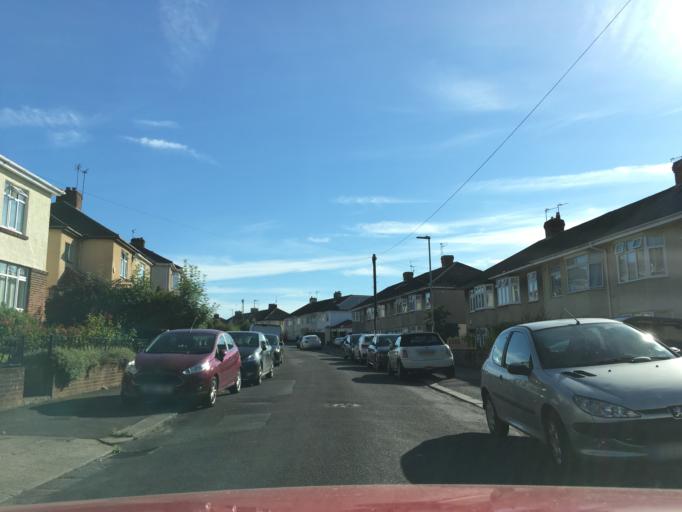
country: GB
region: England
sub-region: Bath and North East Somerset
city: Whitchurch
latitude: 51.4320
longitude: -2.5519
